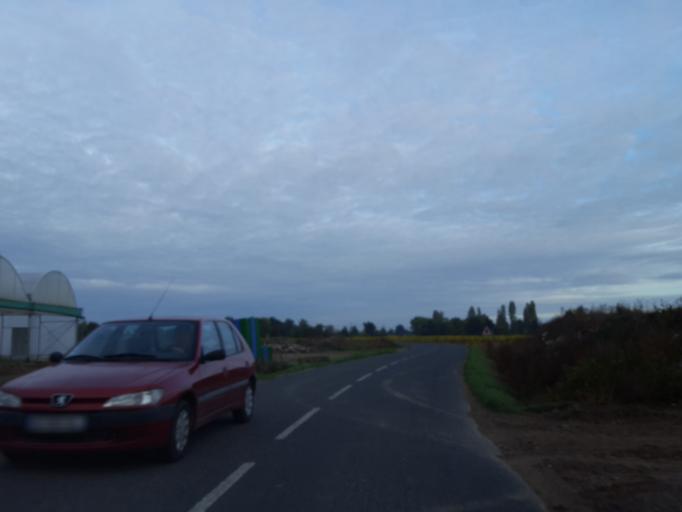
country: FR
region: Pays de la Loire
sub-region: Departement de la Loire-Atlantique
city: Saint-Julien-de-Concelles
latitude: 47.2382
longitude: -1.3900
